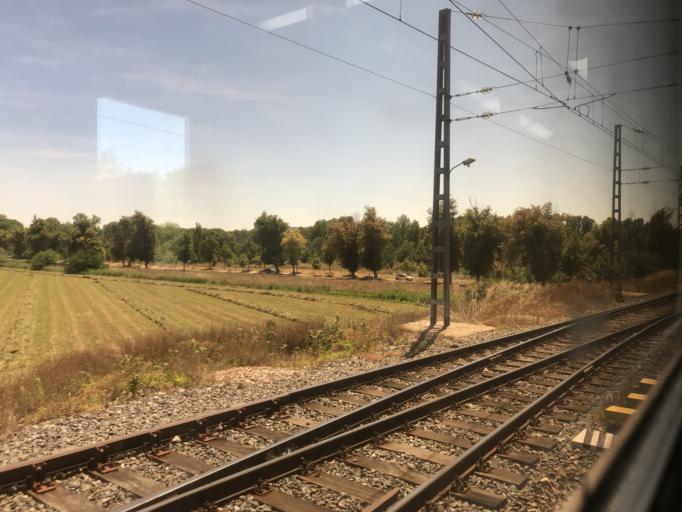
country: ES
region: Madrid
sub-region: Provincia de Madrid
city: Aranjuez
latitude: 40.0394
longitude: -3.6201
